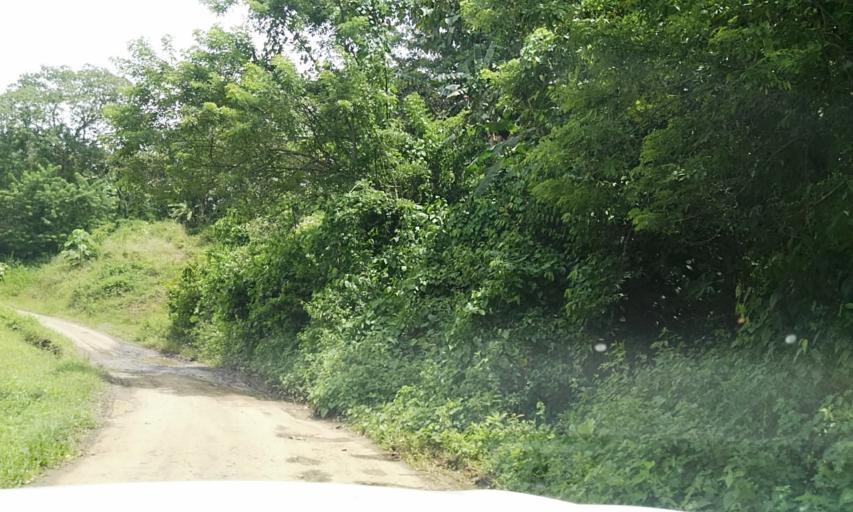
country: NI
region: Matagalpa
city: San Ramon
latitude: 12.9868
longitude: -85.8485
